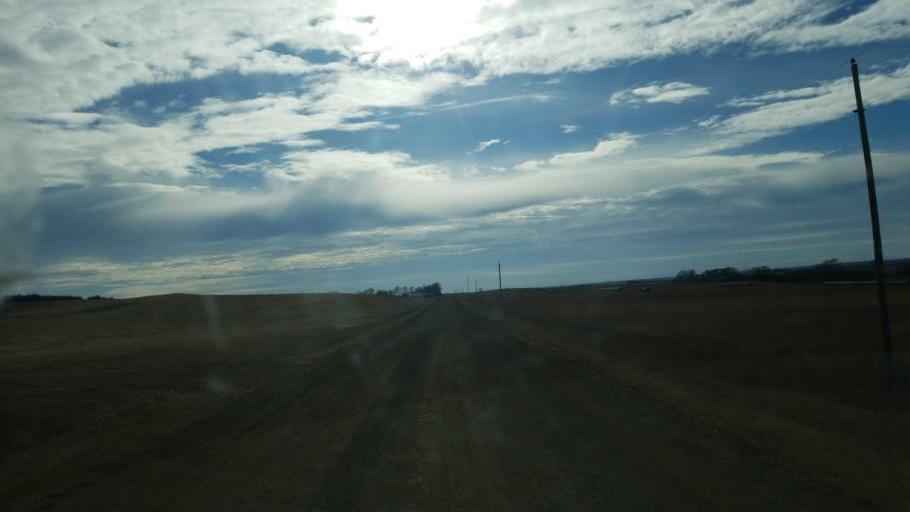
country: US
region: South Dakota
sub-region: Charles Mix County
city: Wagner
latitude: 42.9080
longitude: -98.1705
